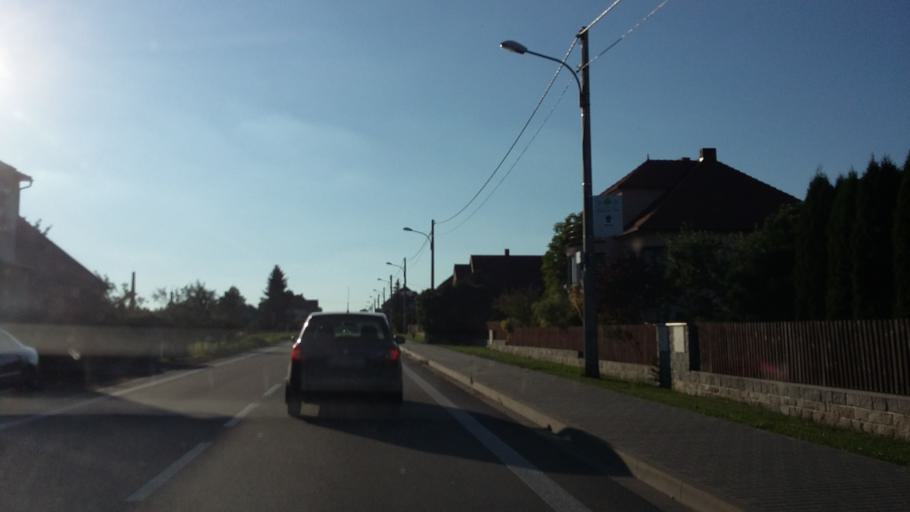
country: CZ
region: Vysocina
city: Merin
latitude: 49.3888
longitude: 15.8976
